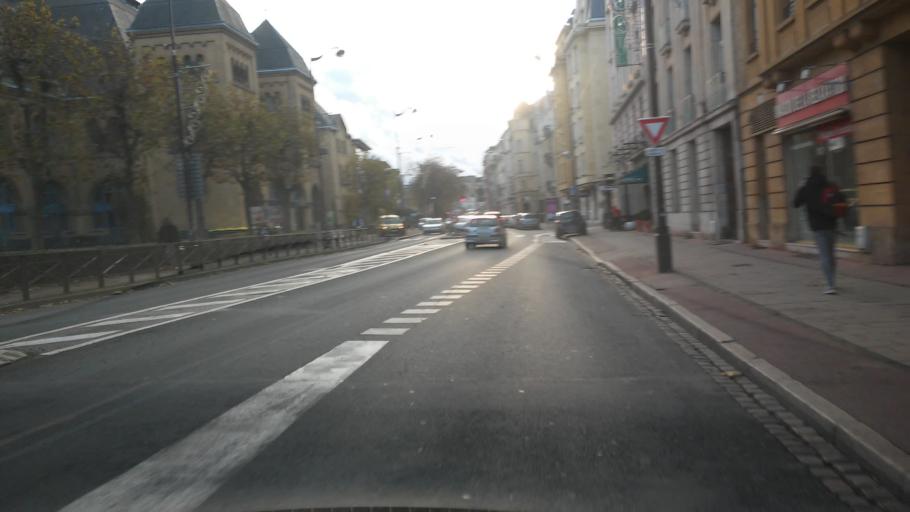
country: FR
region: Lorraine
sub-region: Departement de la Moselle
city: Metz
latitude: 49.1090
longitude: 6.1748
